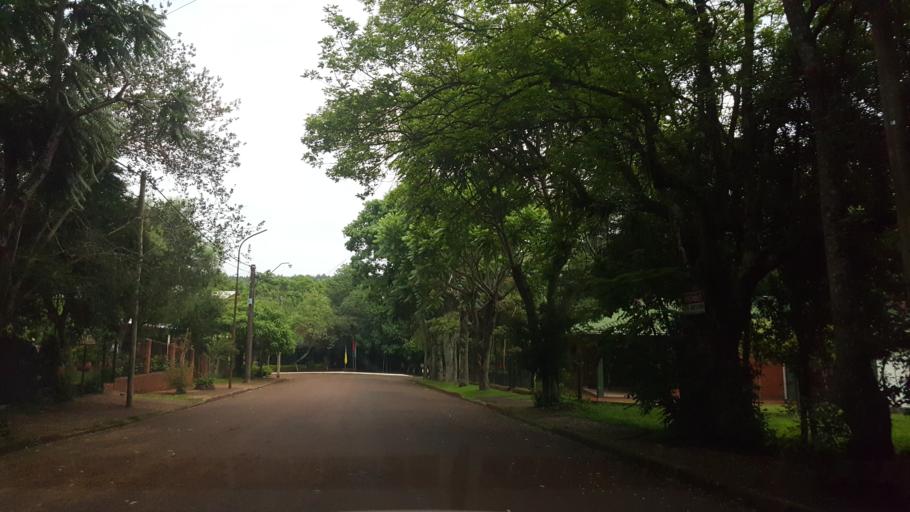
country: AR
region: Misiones
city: Capiovi
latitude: -26.9249
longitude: -55.0609
